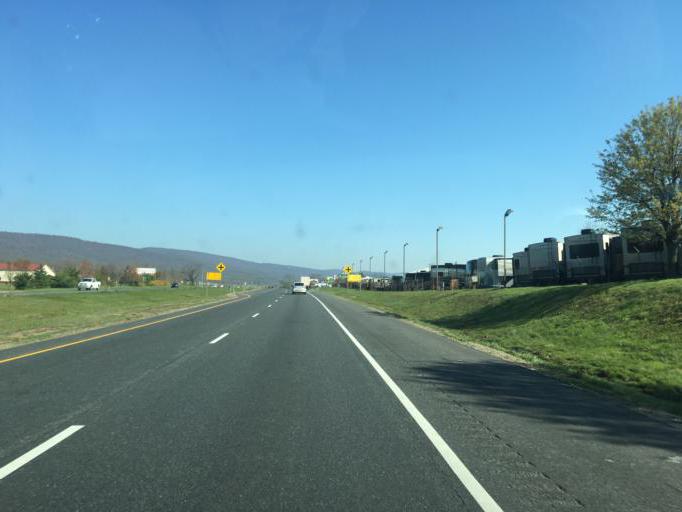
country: US
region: Maryland
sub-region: Frederick County
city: Thurmont
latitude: 39.5416
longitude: -77.4251
